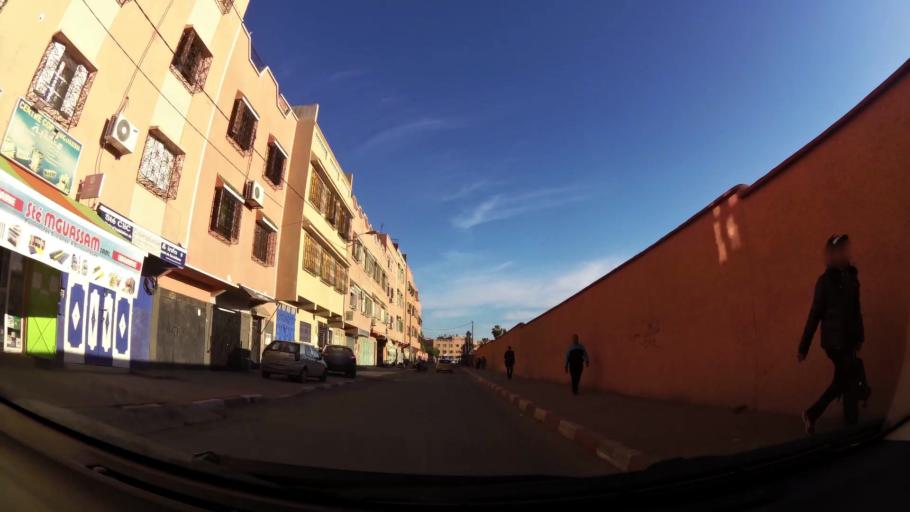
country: MA
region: Marrakech-Tensift-Al Haouz
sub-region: Marrakech
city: Marrakesh
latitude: 31.6216
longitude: -8.0519
